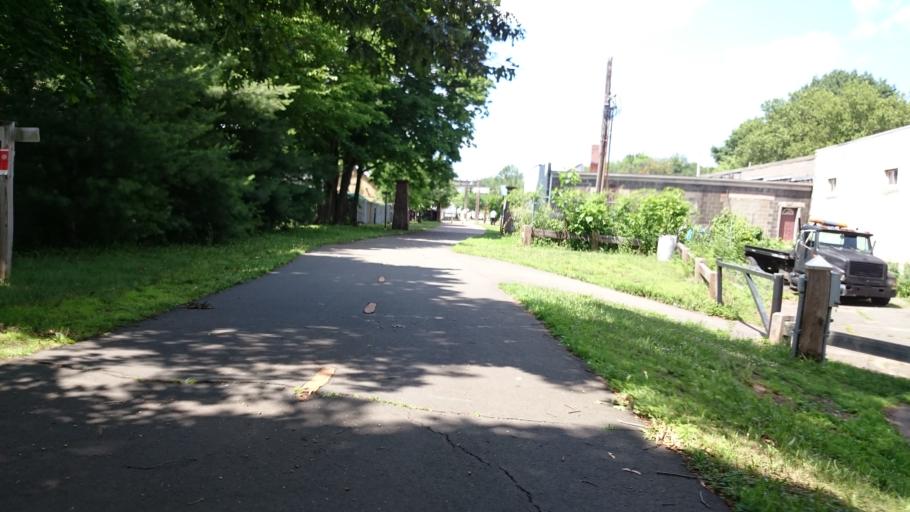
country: US
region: Connecticut
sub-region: New Haven County
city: New Haven
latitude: 41.3350
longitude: -72.9347
